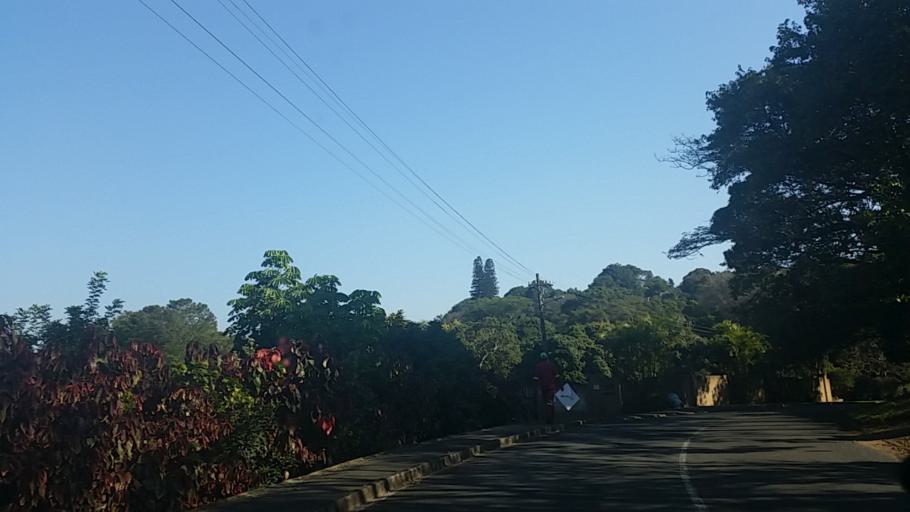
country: ZA
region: KwaZulu-Natal
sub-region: eThekwini Metropolitan Municipality
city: Berea
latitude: -29.8435
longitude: 30.9150
